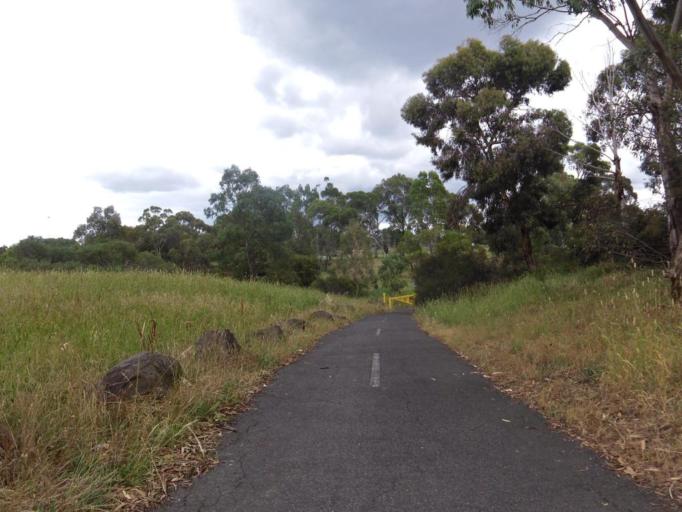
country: AU
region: Victoria
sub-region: Darebin
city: Kingsbury
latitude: -37.7209
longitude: 145.0352
